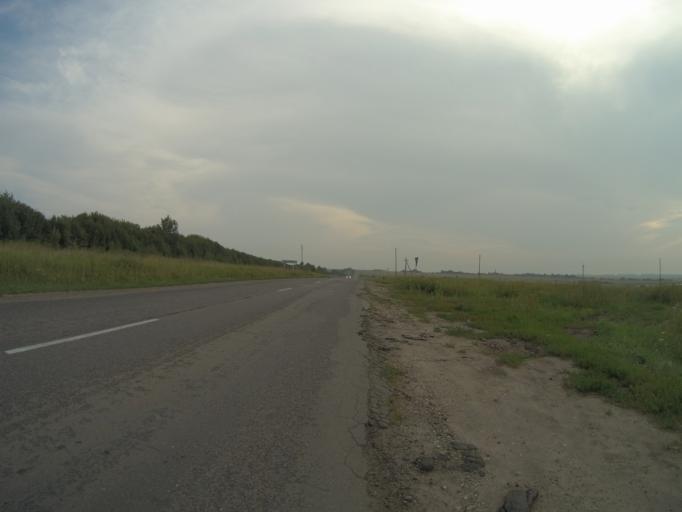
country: RU
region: Vladimir
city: Suzdal'
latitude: 56.3852
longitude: 40.2759
